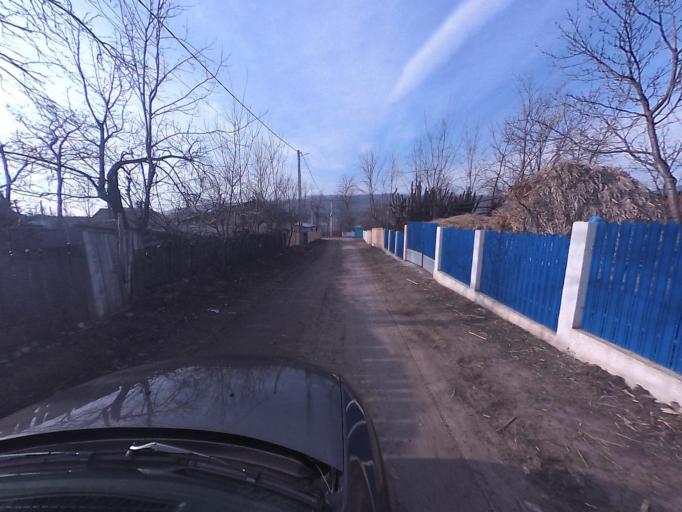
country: RO
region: Vaslui
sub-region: Comuna Solesti
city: Solesti
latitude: 46.8072
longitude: 27.7835
